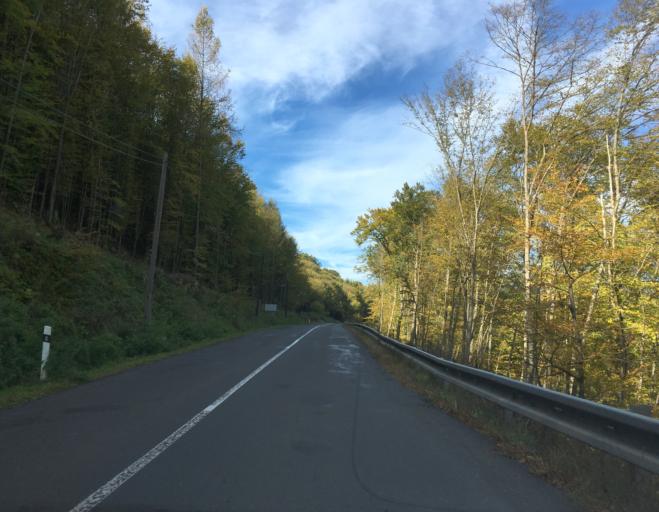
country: SK
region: Banskobystricky
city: Krupina
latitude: 48.3281
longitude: 18.9767
